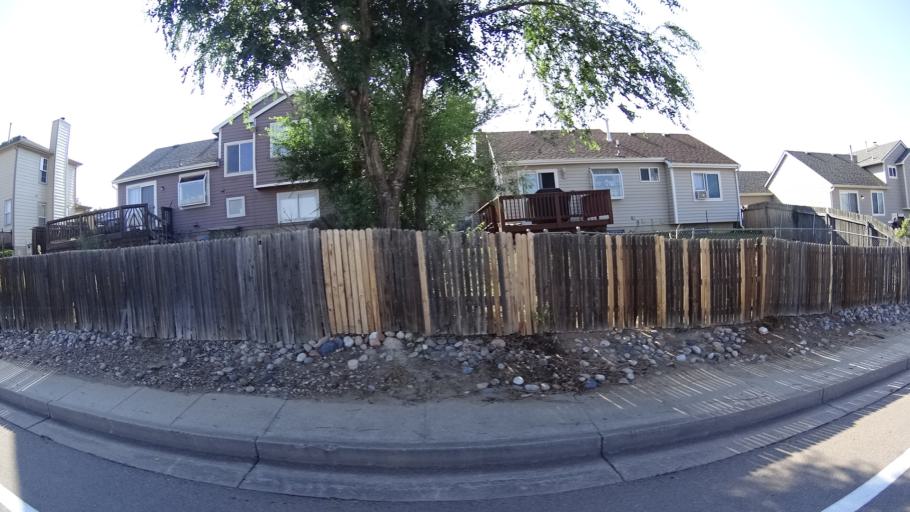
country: US
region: Colorado
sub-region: El Paso County
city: Black Forest
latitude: 38.9460
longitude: -104.7634
